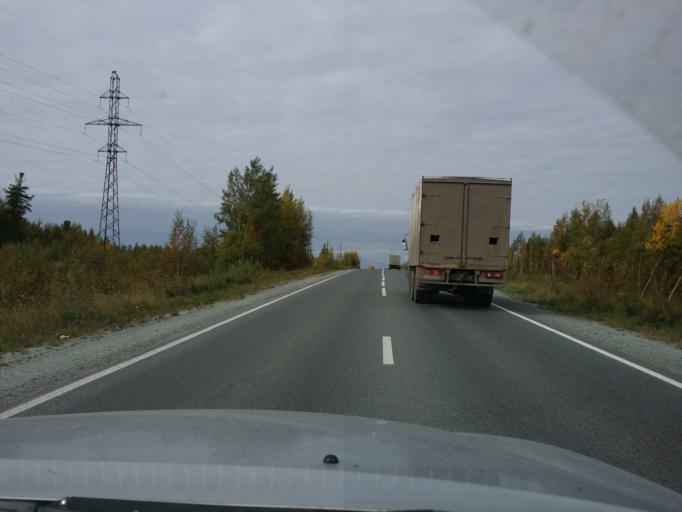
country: RU
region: Khanty-Mansiyskiy Avtonomnyy Okrug
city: Megion
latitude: 61.1028
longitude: 75.9515
